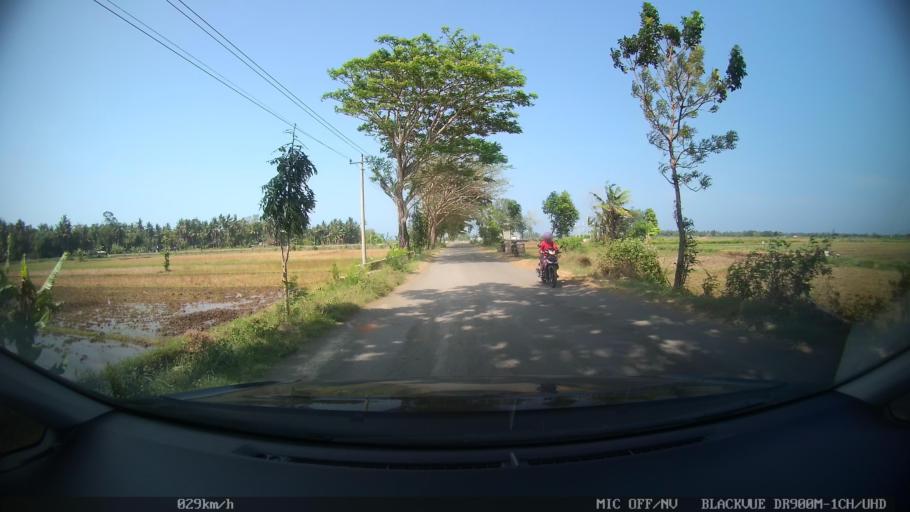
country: ID
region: Daerah Istimewa Yogyakarta
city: Srandakan
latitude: -7.9640
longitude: 110.2139
